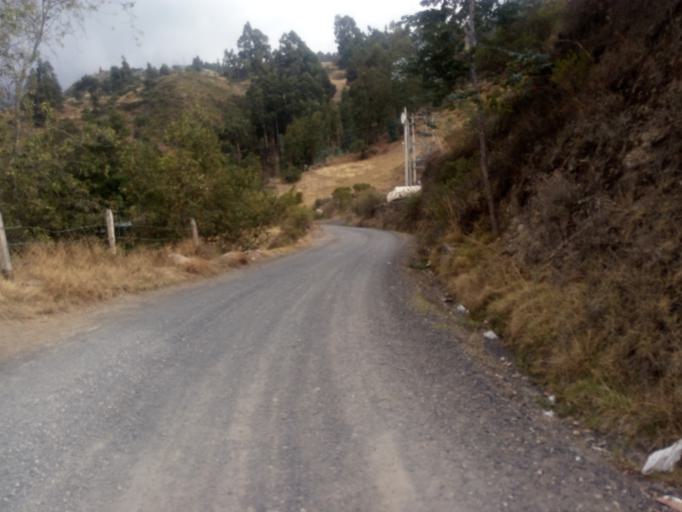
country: CO
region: Boyaca
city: Chita
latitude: 6.1904
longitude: -72.4757
